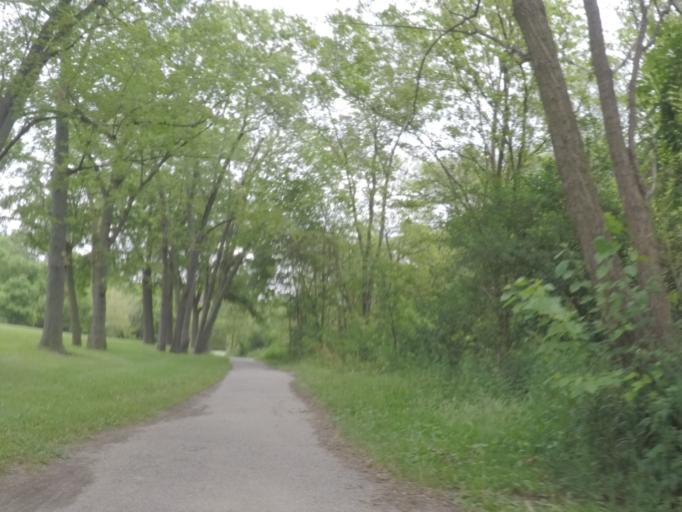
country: CA
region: Ontario
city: Etobicoke
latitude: 43.6583
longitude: -79.5550
